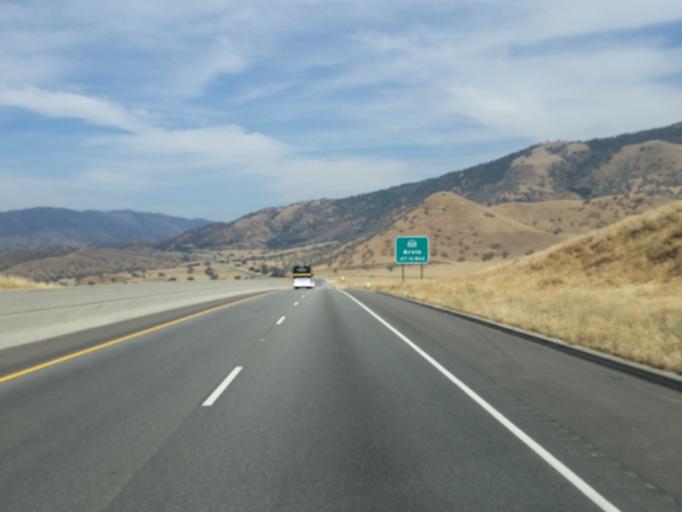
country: US
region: California
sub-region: Kern County
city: Bear Valley Springs
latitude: 35.2682
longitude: -118.6735
